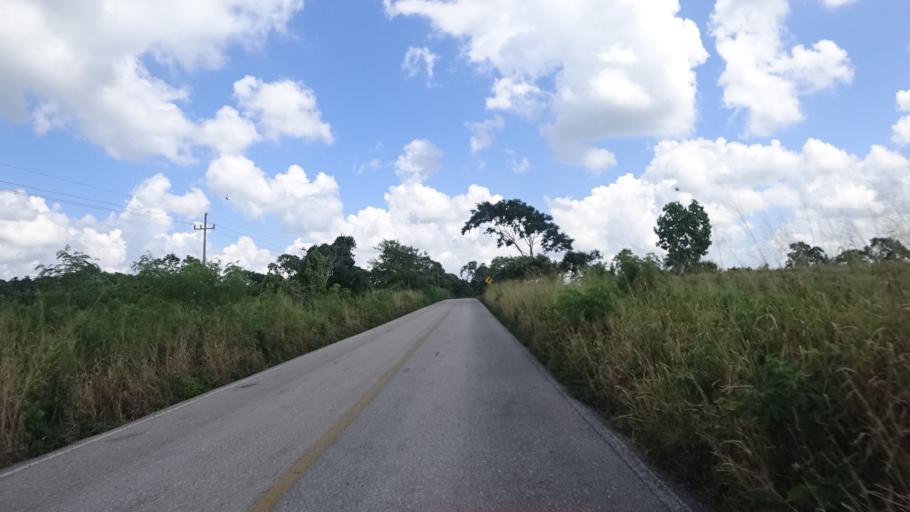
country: MX
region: Yucatan
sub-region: Panaba
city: Loche
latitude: 21.4053
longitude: -88.1429
